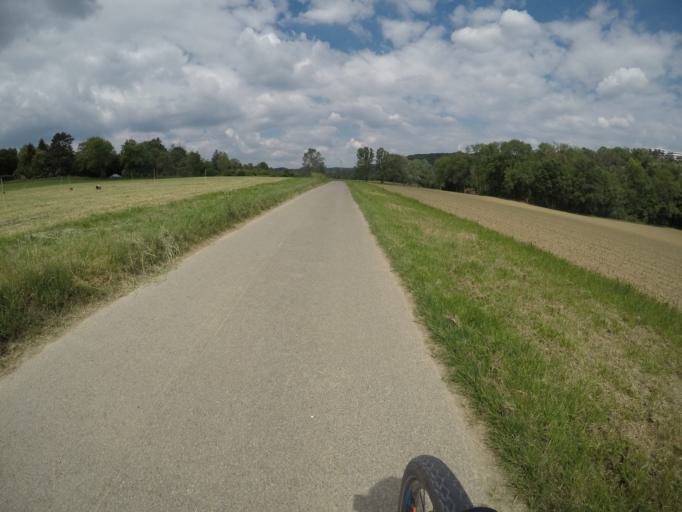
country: DE
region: Baden-Wuerttemberg
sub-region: Regierungsbezirk Stuttgart
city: Ostfildern
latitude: 48.7183
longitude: 9.2182
